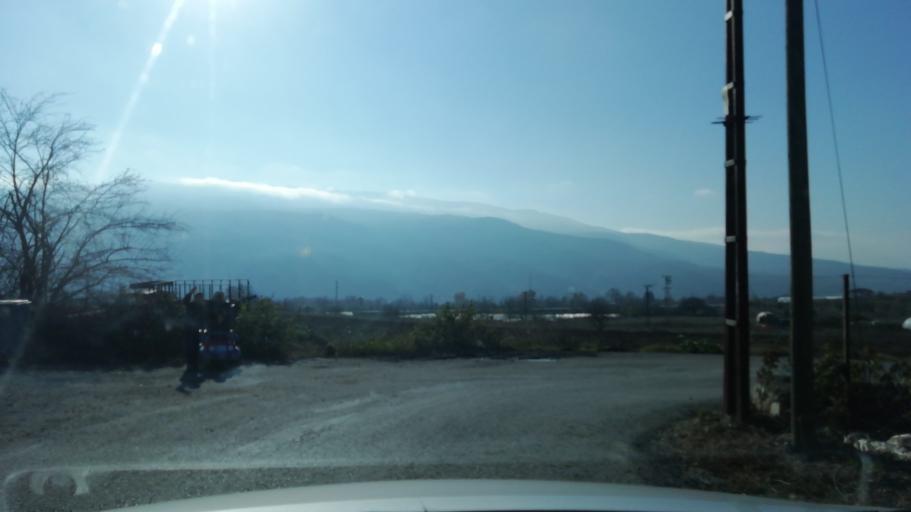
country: TR
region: Karabuk
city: Safranbolu
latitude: 41.2264
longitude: 32.7835
